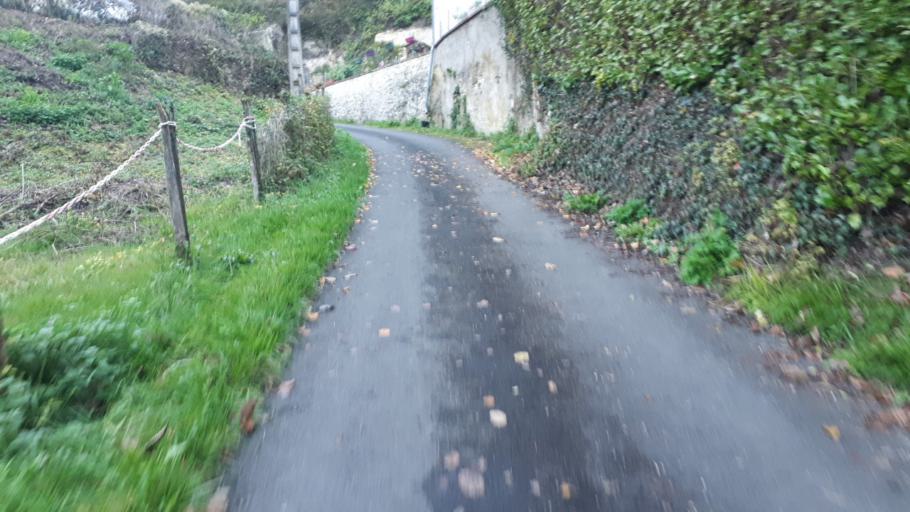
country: FR
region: Centre
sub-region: Departement du Loir-et-Cher
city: Lunay
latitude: 47.7697
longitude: 0.9266
